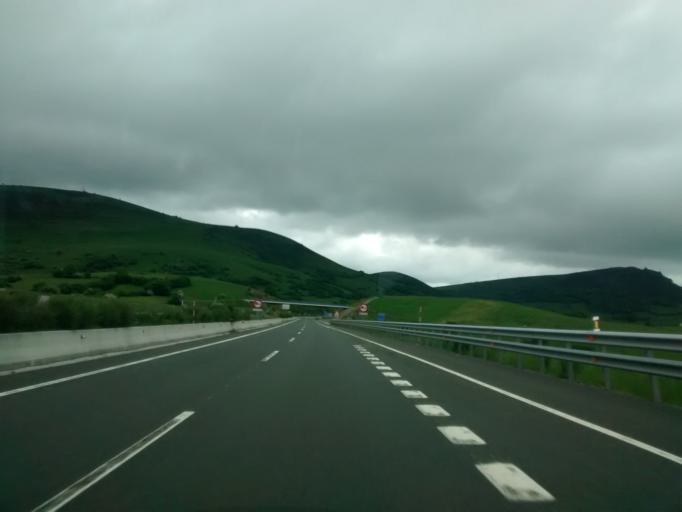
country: ES
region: Cantabria
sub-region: Provincia de Cantabria
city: Pesquera
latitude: 43.0732
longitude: -4.0856
